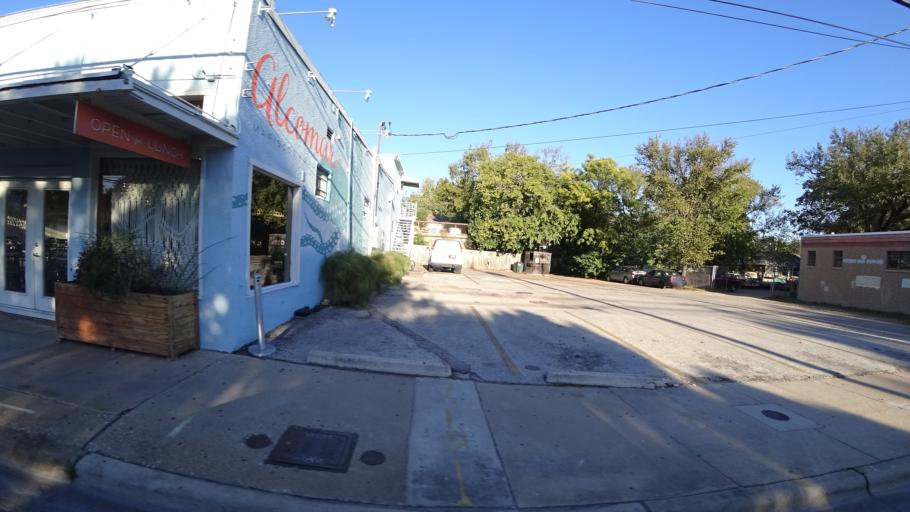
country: US
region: Texas
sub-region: Travis County
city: Austin
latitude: 30.2469
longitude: -97.7562
